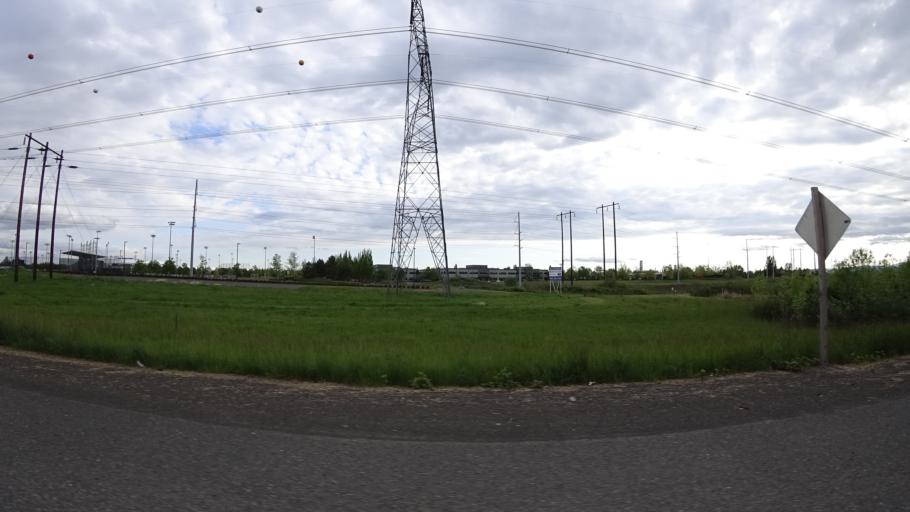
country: US
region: Oregon
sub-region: Washington County
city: Rockcreek
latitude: 45.5579
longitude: -122.9104
